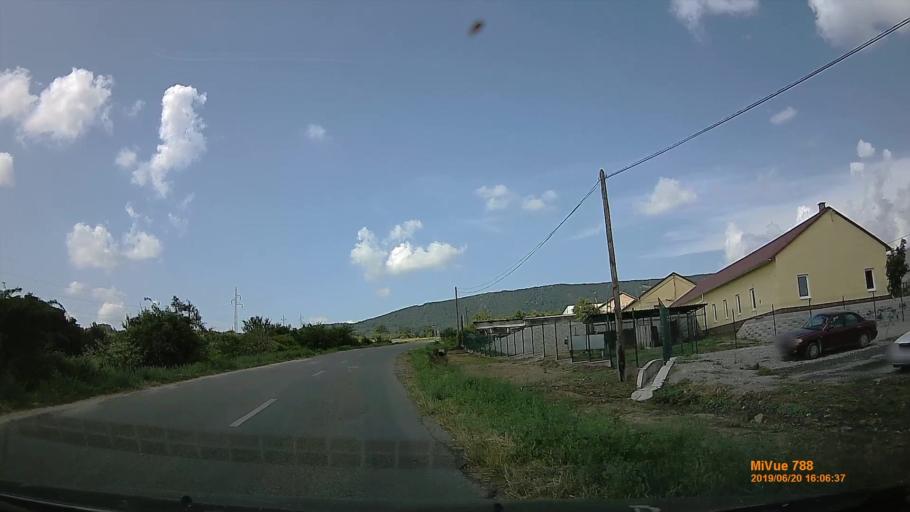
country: HU
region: Baranya
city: Pellerd
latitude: 46.0815
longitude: 18.1098
